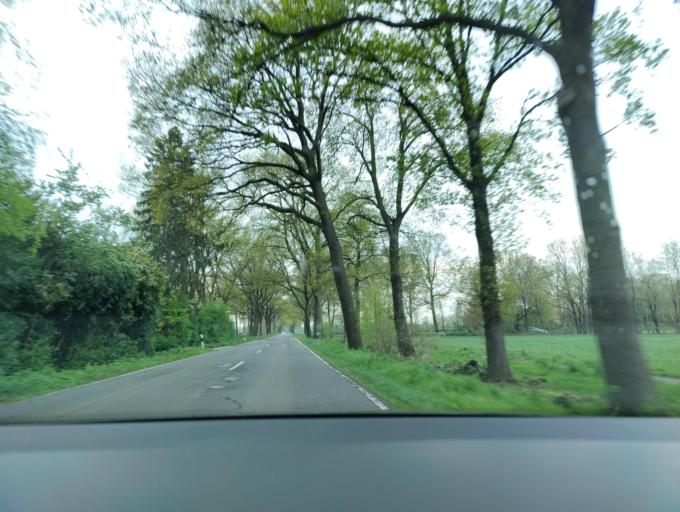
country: DE
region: Lower Saxony
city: Wietmarschen
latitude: 52.5035
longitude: 7.1800
